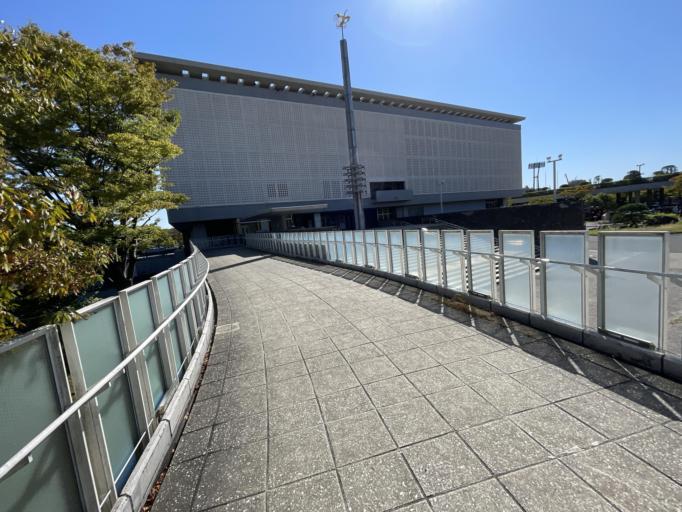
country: JP
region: Niigata
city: Niigata-shi
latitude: 37.9139
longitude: 139.0393
